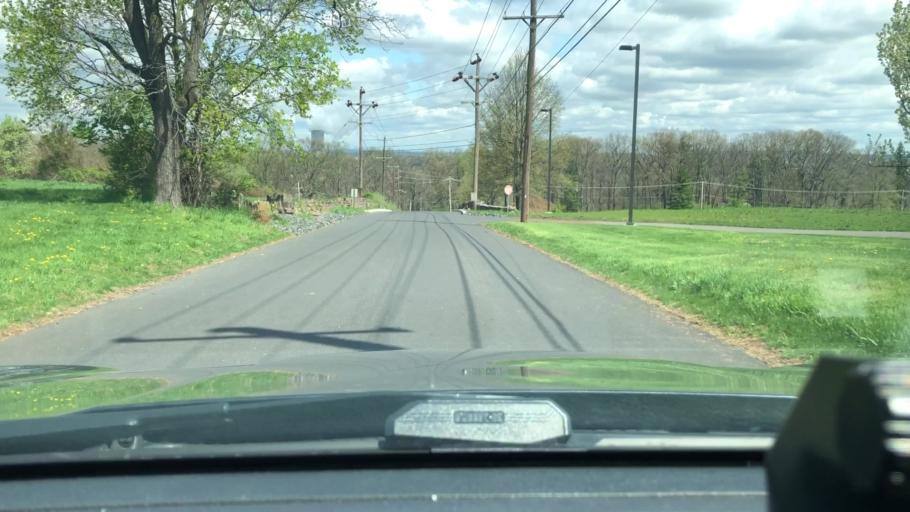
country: US
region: Pennsylvania
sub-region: Chester County
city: Spring City
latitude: 40.1897
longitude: -75.5666
